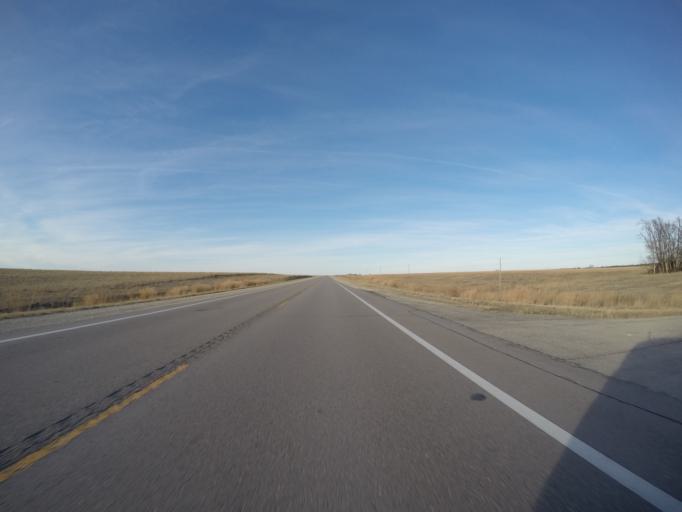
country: US
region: Kansas
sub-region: Marion County
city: Marion
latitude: 38.3289
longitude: -96.9667
